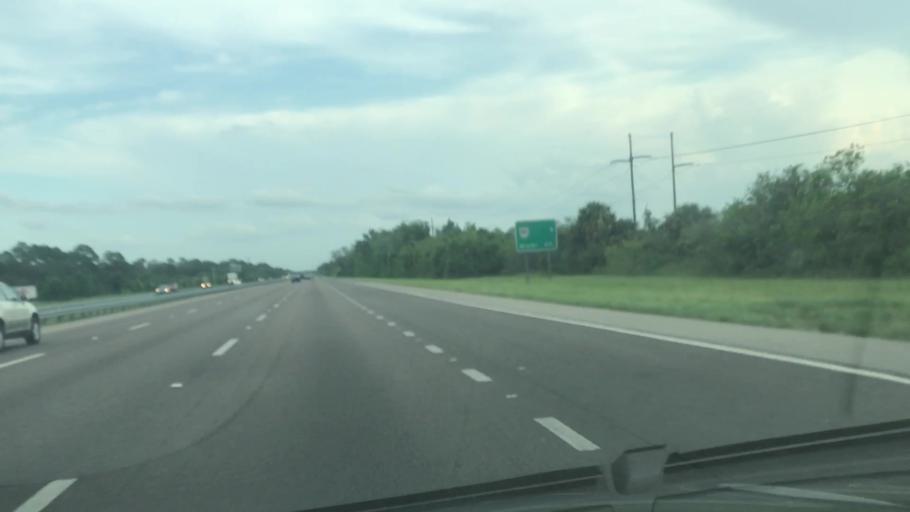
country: US
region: Florida
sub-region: Brevard County
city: Port Saint John
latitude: 28.4999
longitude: -80.8384
